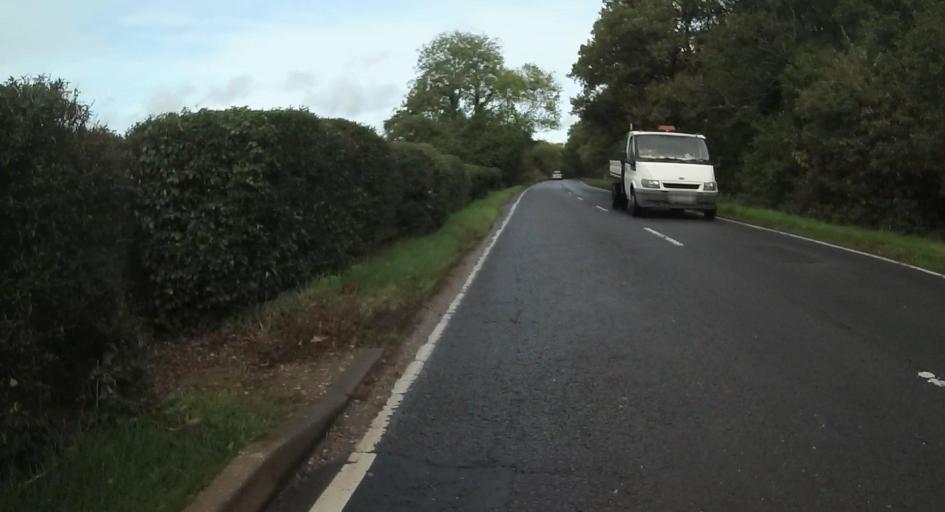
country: GB
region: England
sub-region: Hampshire
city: Odiham
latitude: 51.2677
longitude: -0.9275
